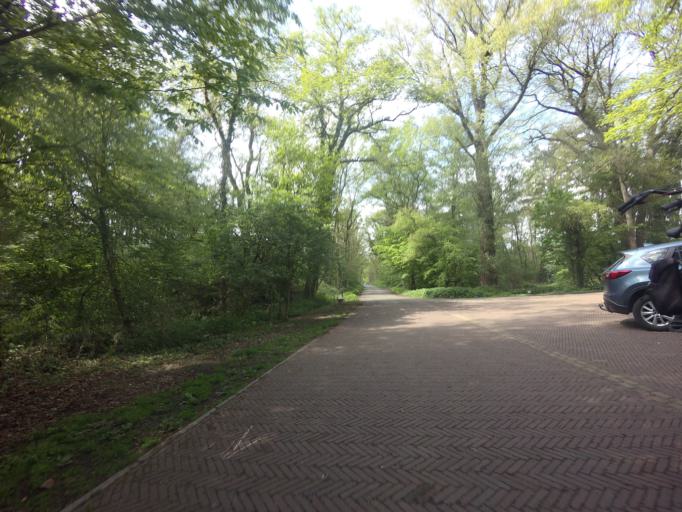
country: NL
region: Overijssel
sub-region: Gemeente Haaksbergen
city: Haaksbergen
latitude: 52.1371
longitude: 6.7307
